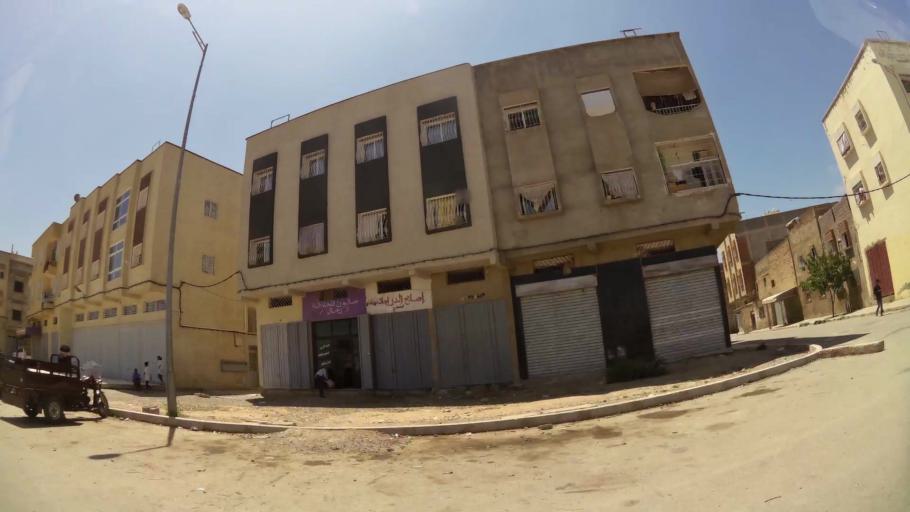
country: MA
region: Fes-Boulemane
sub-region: Fes
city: Fes
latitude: 34.0360
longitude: -5.0472
